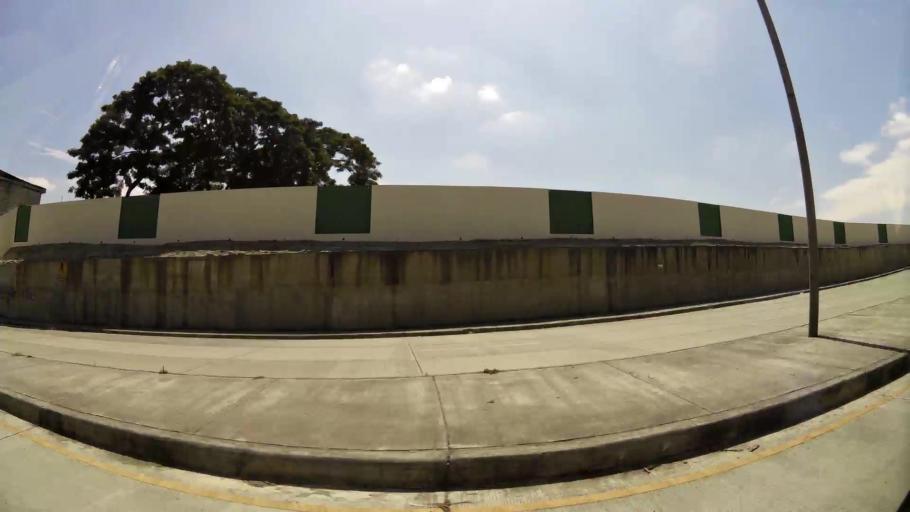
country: EC
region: Guayas
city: Guayaquil
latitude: -2.1348
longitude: -79.9201
